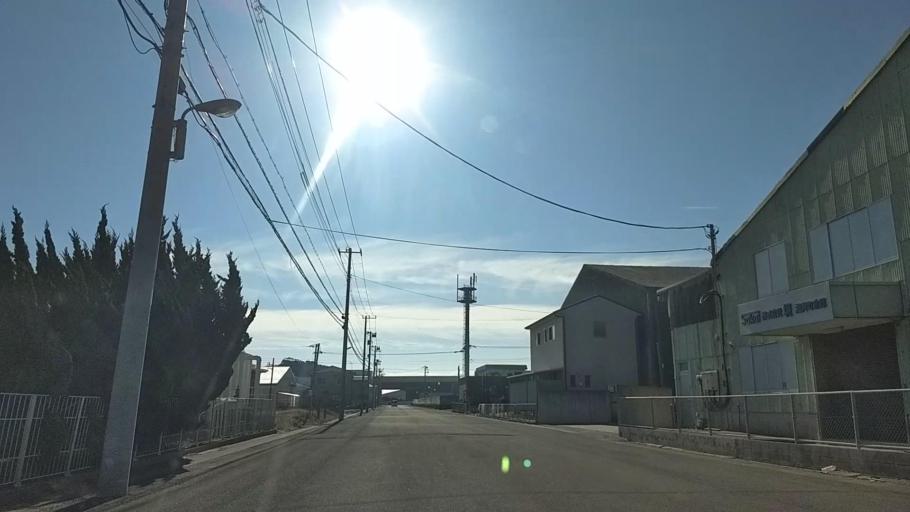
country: JP
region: Chiba
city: Hasaki
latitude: 35.7036
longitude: 140.8459
